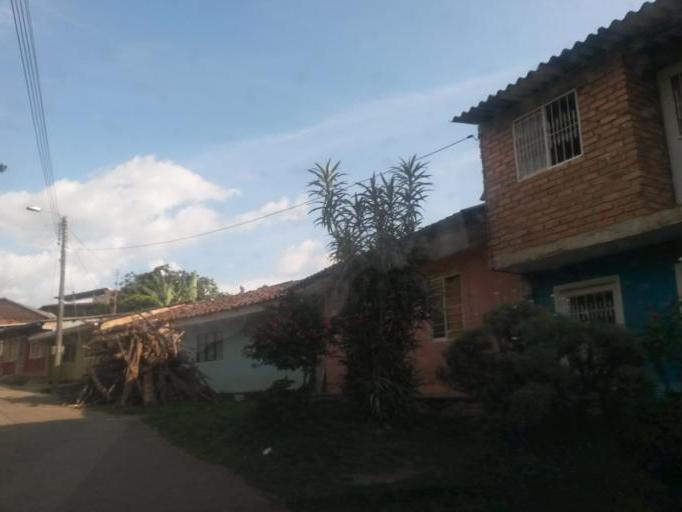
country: CO
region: Cauca
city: El Tambo
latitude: 2.4527
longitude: -76.8134
